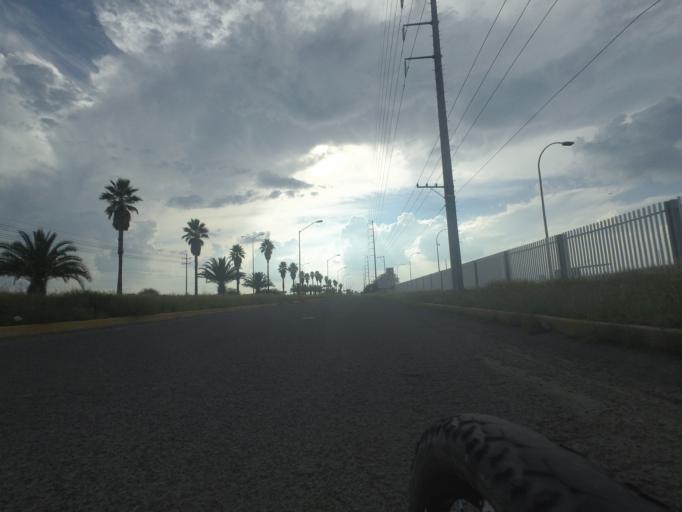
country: MX
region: Aguascalientes
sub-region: Aguascalientes
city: Penuelas (El Cienegal)
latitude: 21.7254
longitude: -102.2998
